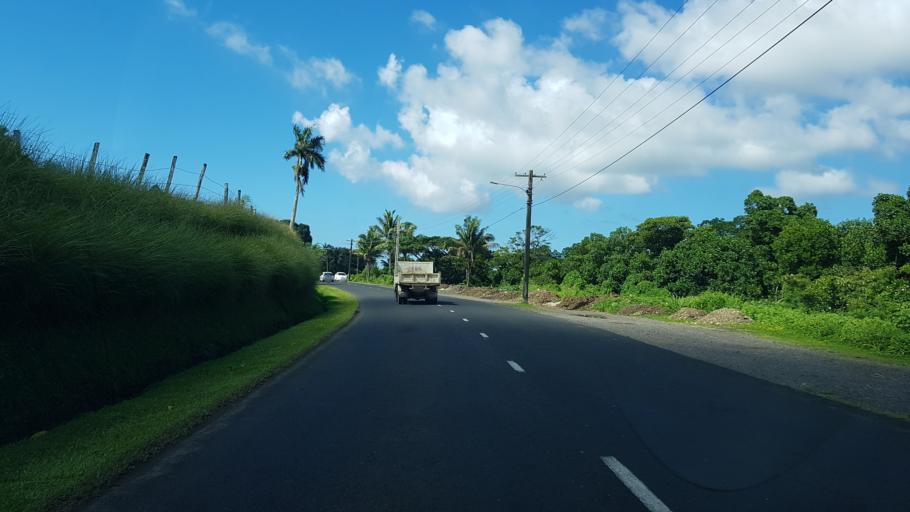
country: FJ
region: Central
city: Suva
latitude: -18.1406
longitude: 178.4565
